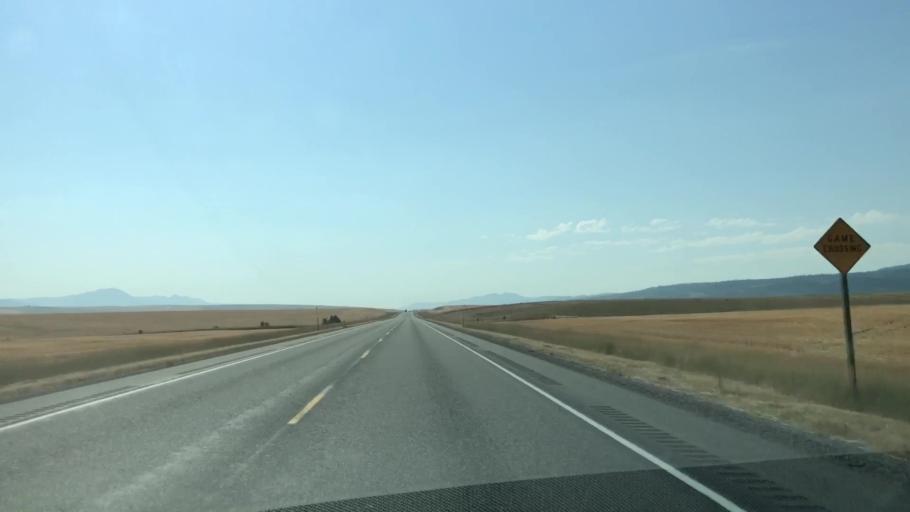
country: US
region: Idaho
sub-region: Madison County
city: Rexburg
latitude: 43.5609
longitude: -111.5444
